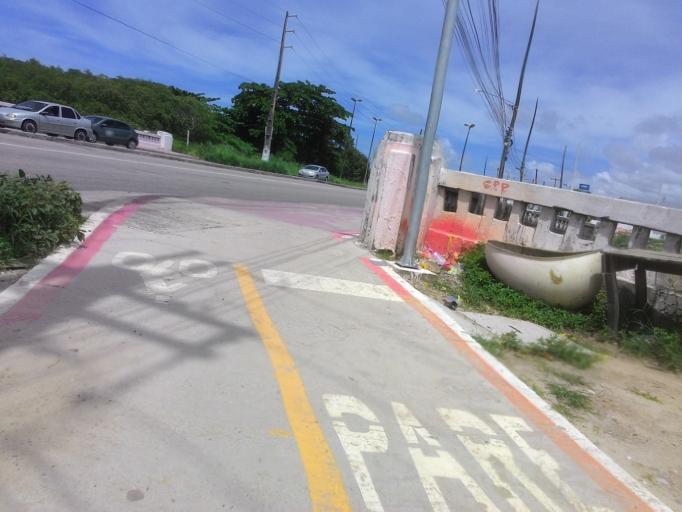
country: BR
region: Pernambuco
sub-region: Olinda
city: Olinda
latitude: -8.0241
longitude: -34.8628
